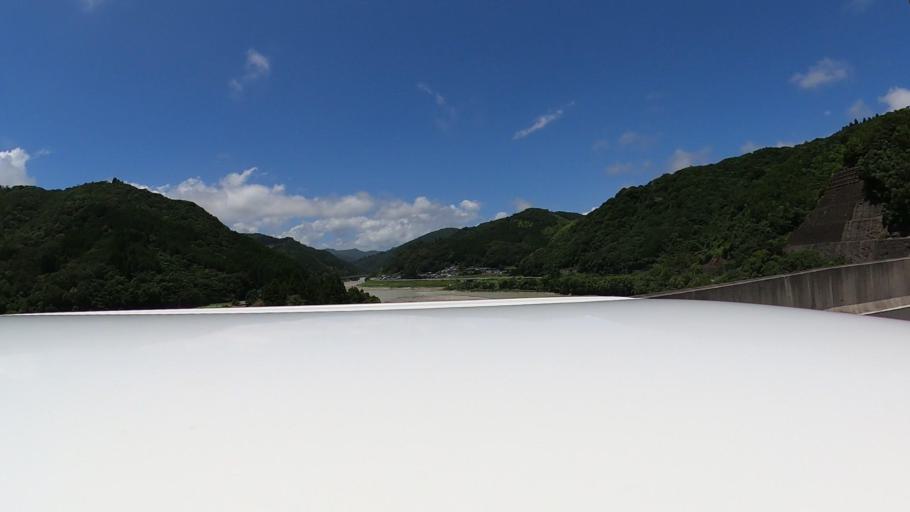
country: JP
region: Miyazaki
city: Takanabe
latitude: 32.3435
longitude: 131.5990
